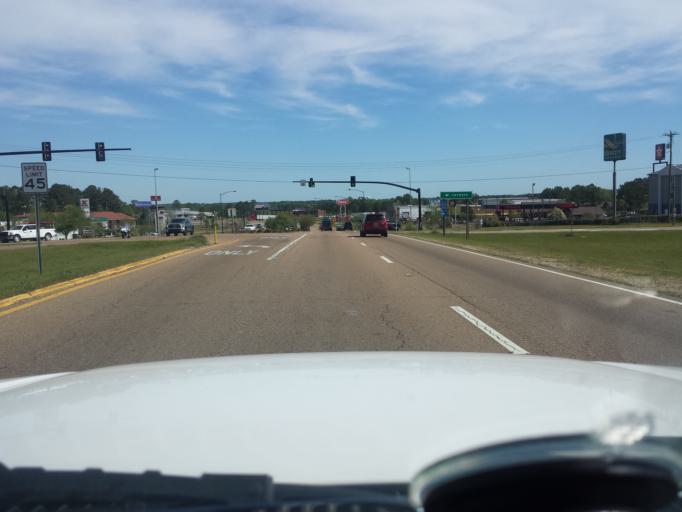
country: US
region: Mississippi
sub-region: Rankin County
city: Pearl
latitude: 32.2720
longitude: -90.0730
